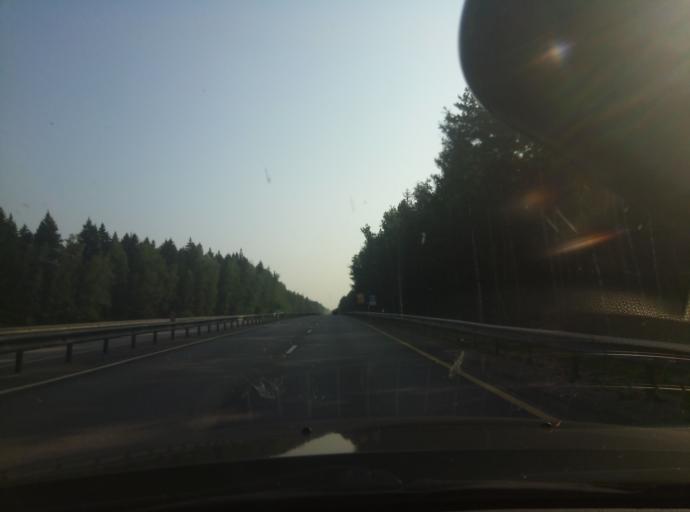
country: RU
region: Kaluga
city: Maloyaroslavets
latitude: 54.9972
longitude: 36.5230
